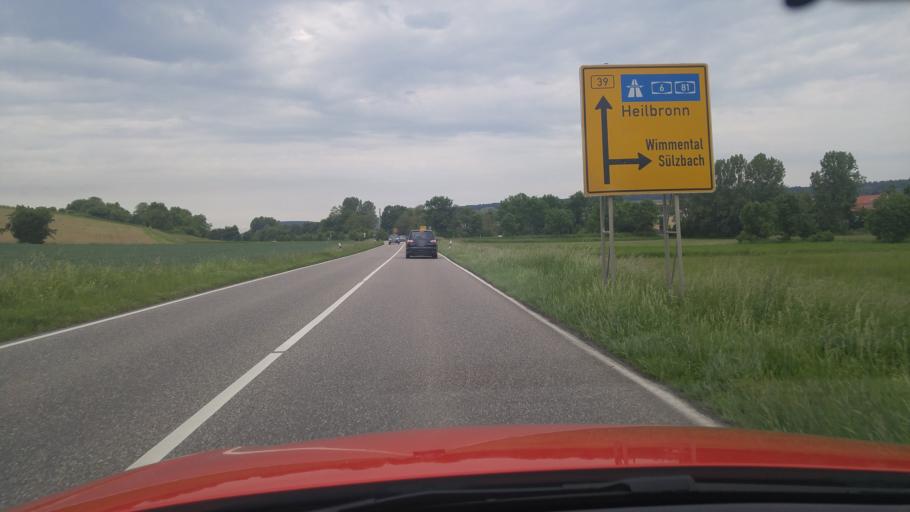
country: DE
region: Baden-Wuerttemberg
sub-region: Regierungsbezirk Stuttgart
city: Lehrensteinsfeld
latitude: 49.1423
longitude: 9.3443
